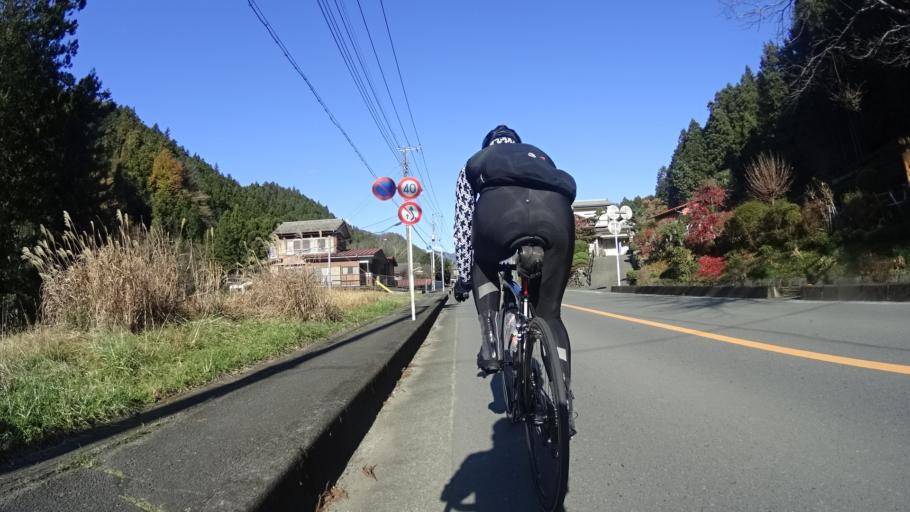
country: JP
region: Tokyo
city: Ome
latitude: 35.8741
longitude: 139.1870
